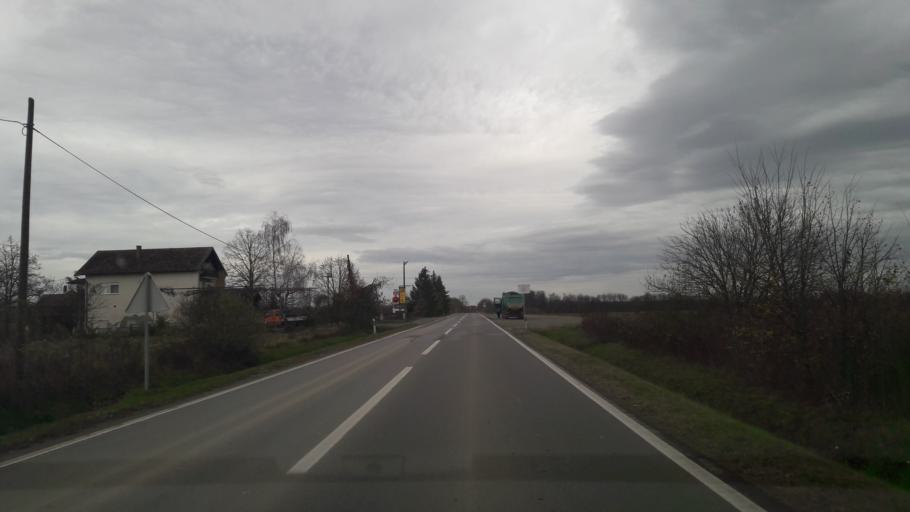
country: HR
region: Osjecko-Baranjska
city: Fericanci
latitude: 45.5329
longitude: 17.9442
